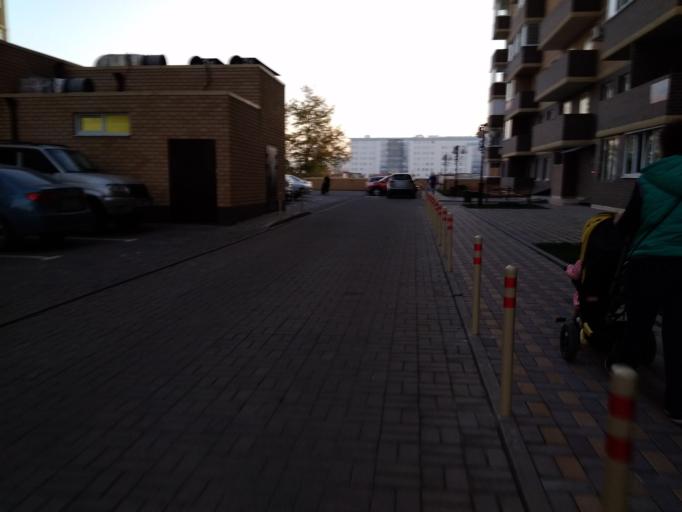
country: RU
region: Krasnodarskiy
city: Krasnodar
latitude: 45.0778
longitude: 39.0035
